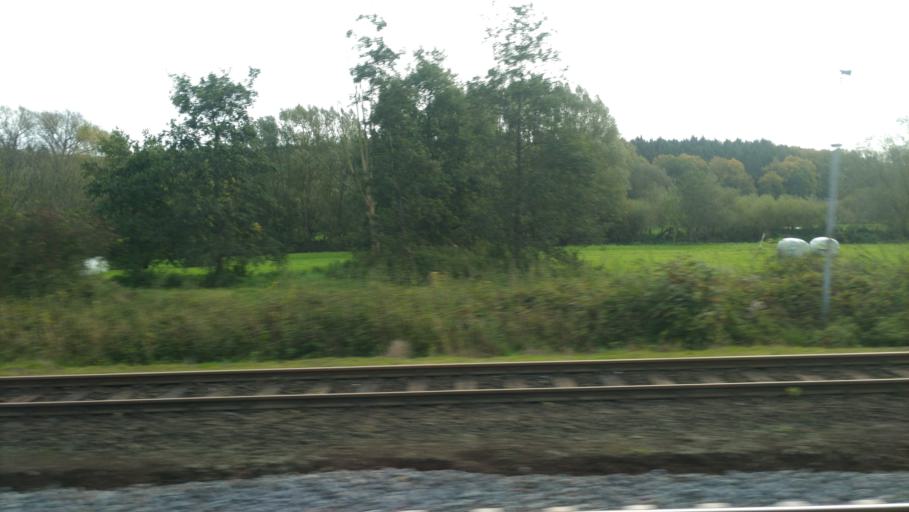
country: DE
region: Lower Saxony
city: Elze
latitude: 52.1289
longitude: 9.7515
